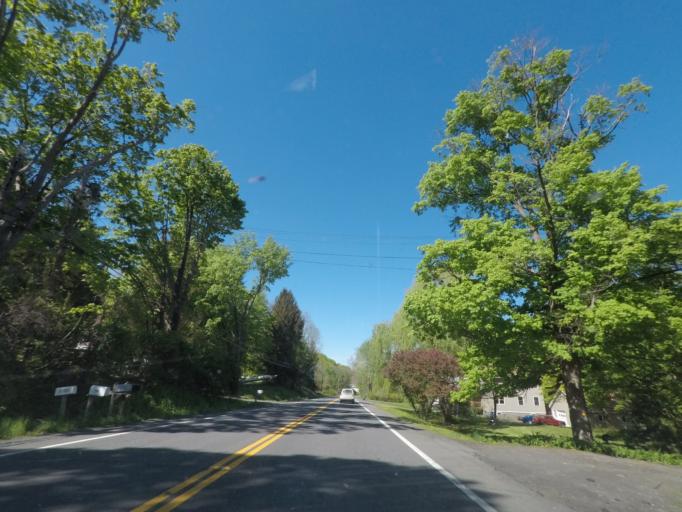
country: US
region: New York
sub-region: Greene County
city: Jefferson Heights
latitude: 42.2504
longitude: -73.8628
